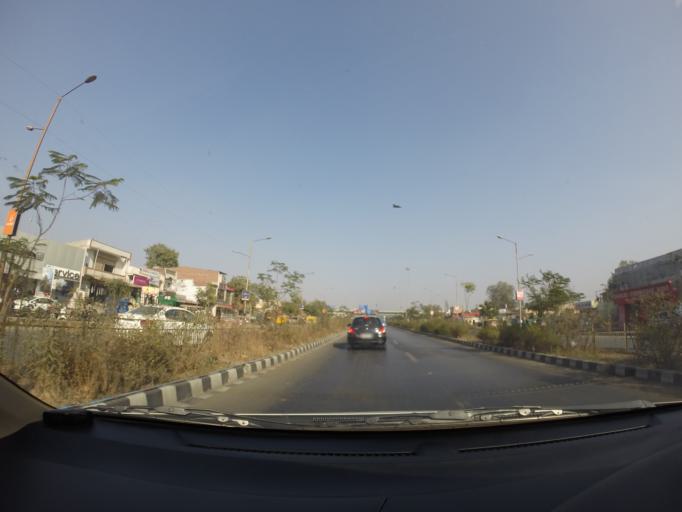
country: IN
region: Gujarat
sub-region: Ahmadabad
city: Ahmedabad
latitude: 22.9756
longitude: 72.6001
